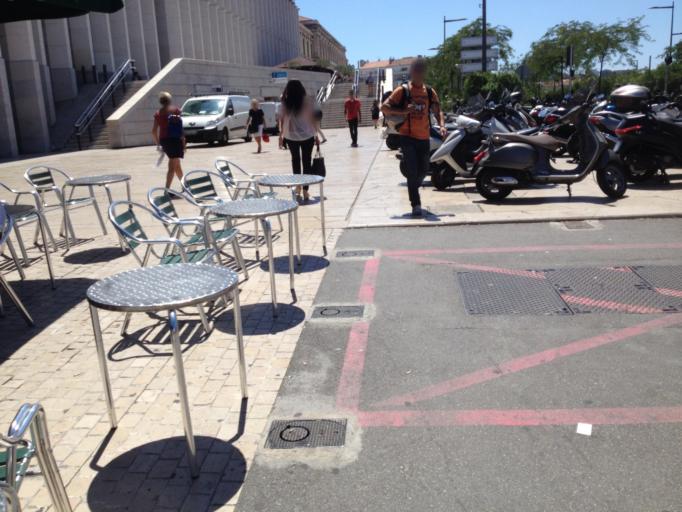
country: FR
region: Provence-Alpes-Cote d'Azur
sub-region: Departement des Bouches-du-Rhone
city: Marseille 03
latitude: 43.3036
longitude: 5.3789
